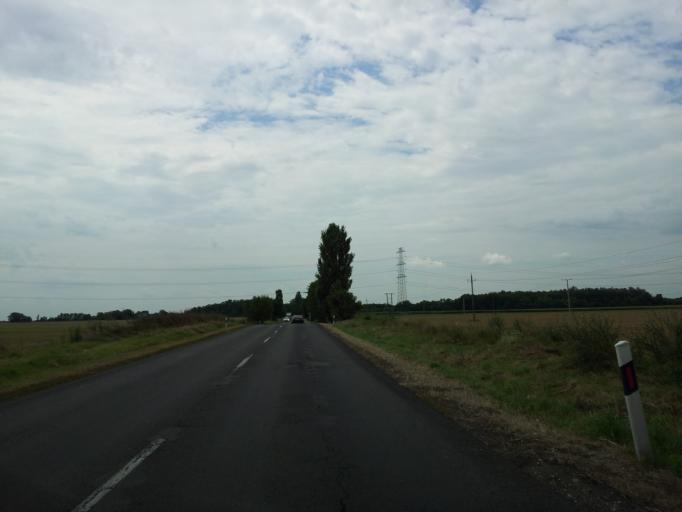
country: HU
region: Pest
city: Dunavarsany
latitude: 47.2465
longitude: 19.0225
